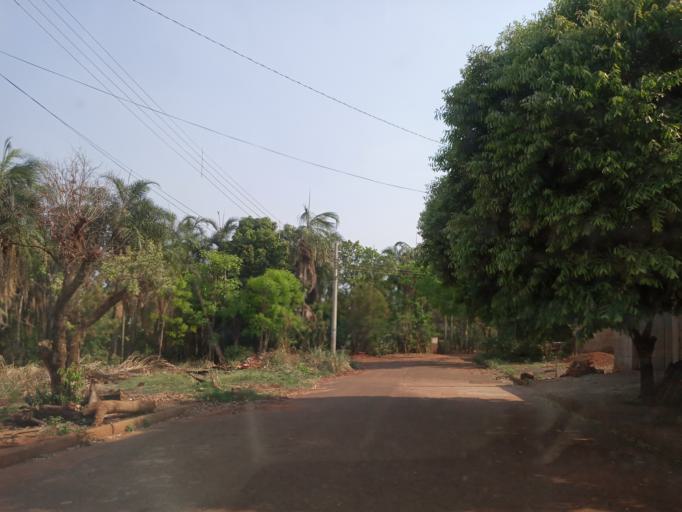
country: BR
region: Minas Gerais
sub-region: Ituiutaba
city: Ituiutaba
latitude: -18.9626
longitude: -49.4790
